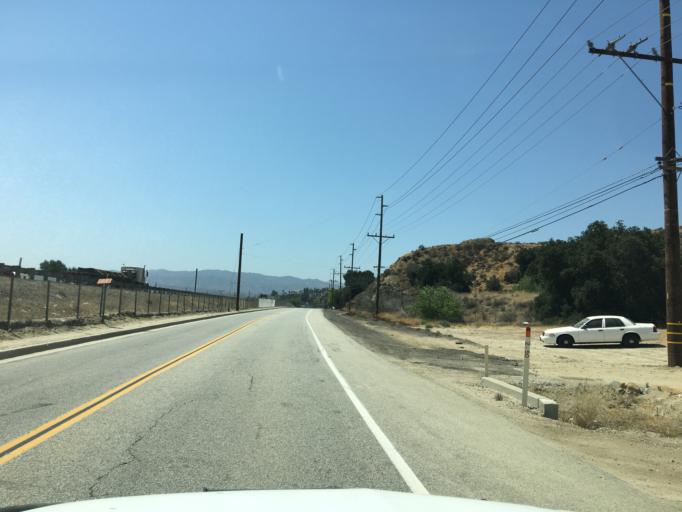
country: US
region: California
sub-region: Los Angeles County
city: Castaic
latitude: 34.4784
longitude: -118.6150
